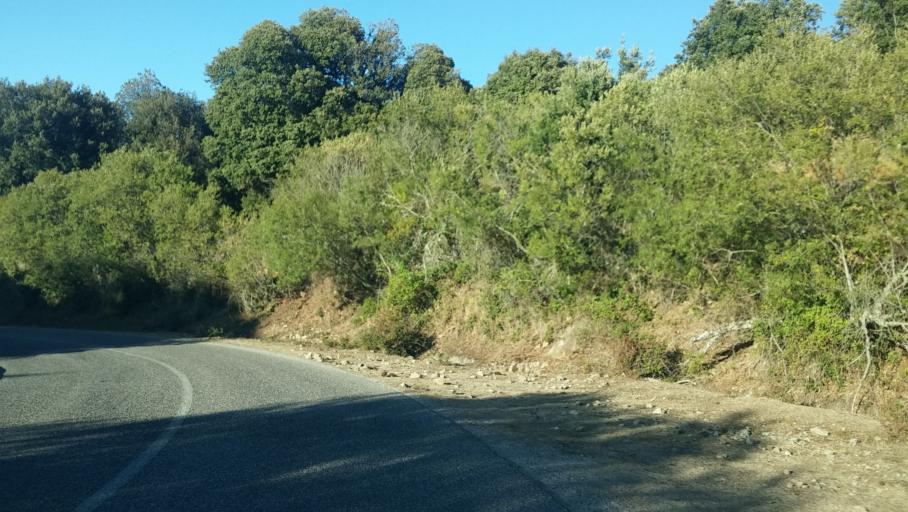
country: IT
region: Sardinia
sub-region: Provincia di Nuoro
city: Orgosolo
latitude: 40.1834
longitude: 9.3500
